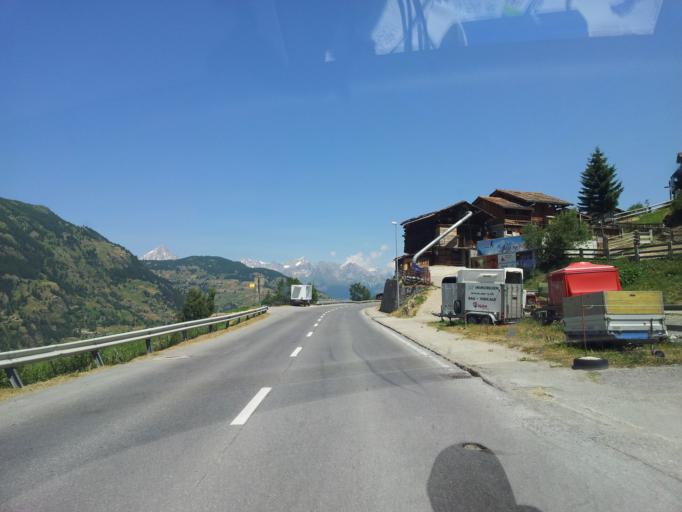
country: CH
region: Valais
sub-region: Visp District
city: Grachen
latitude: 46.1973
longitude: 7.8352
